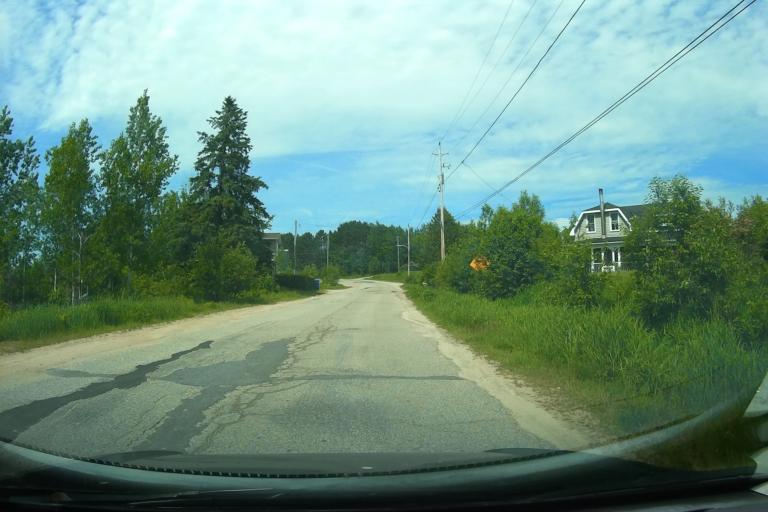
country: CA
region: Ontario
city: Powassan
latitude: 46.2335
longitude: -79.1478
